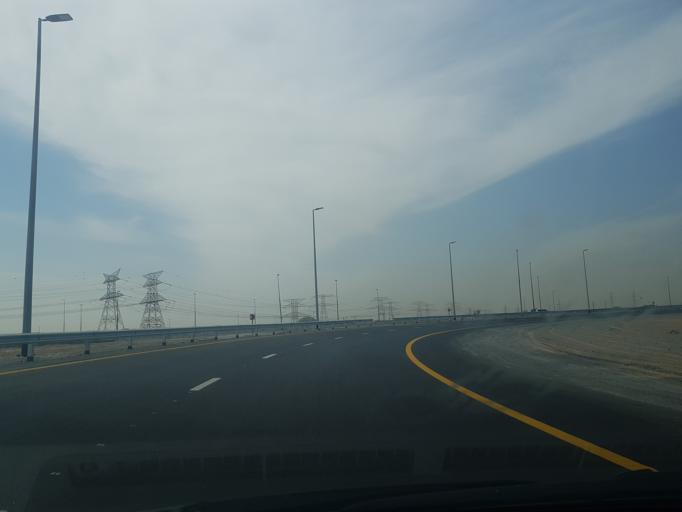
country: AE
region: Ash Shariqah
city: Sharjah
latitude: 25.2363
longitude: 55.5670
